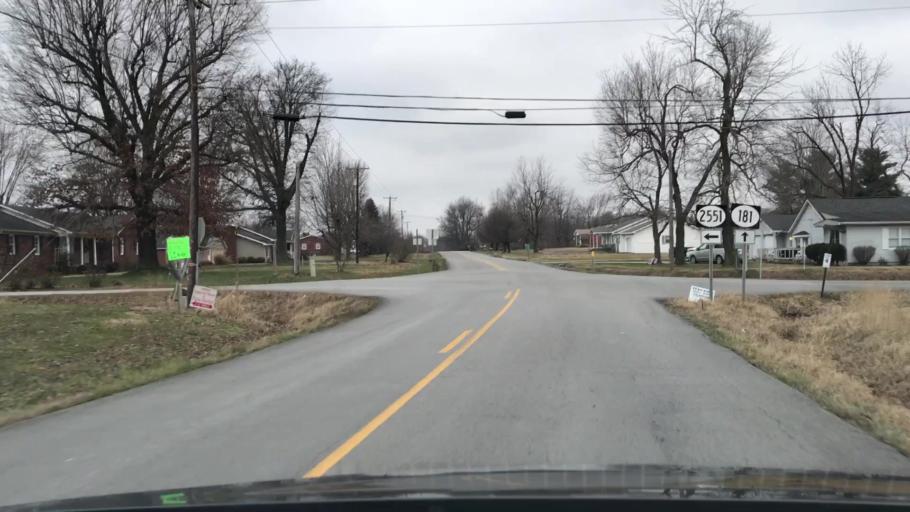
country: US
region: Kentucky
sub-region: Muhlenberg County
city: Morehead
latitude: 37.3564
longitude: -87.2296
